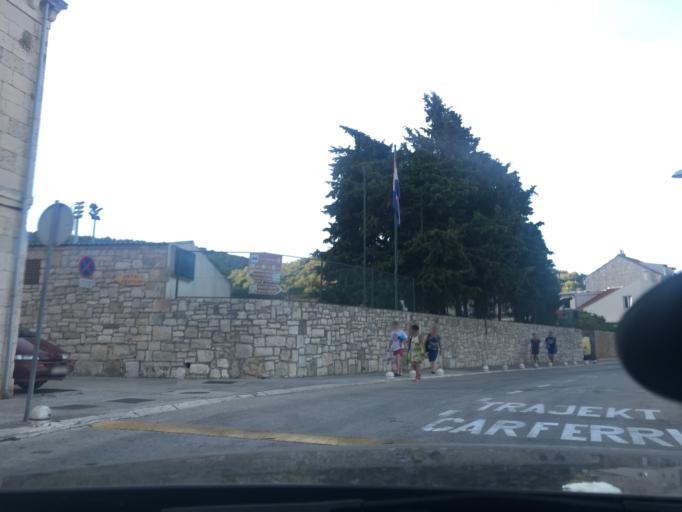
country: HR
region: Splitsko-Dalmatinska
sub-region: Grad Vis
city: Vis
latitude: 43.0627
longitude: 16.1841
